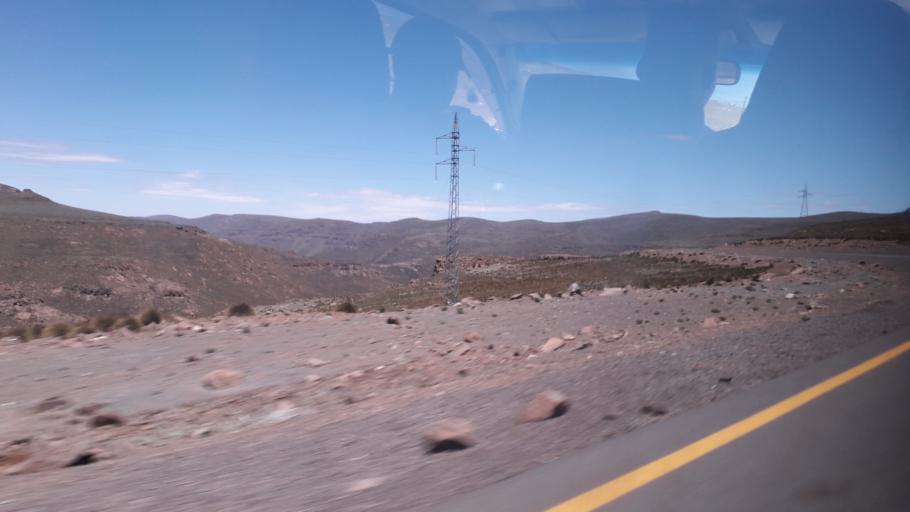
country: ZA
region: Orange Free State
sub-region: Thabo Mofutsanyana District Municipality
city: Phuthaditjhaba
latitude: -28.8351
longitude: 28.7445
